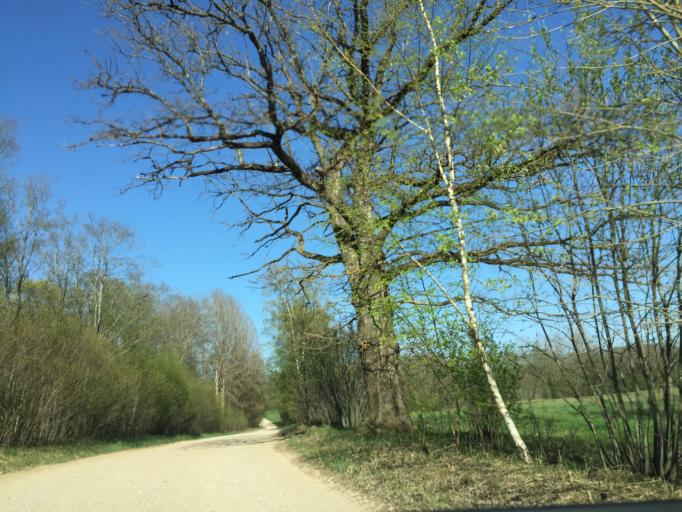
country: LV
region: Ergli
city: Ergli
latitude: 56.9031
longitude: 25.4319
